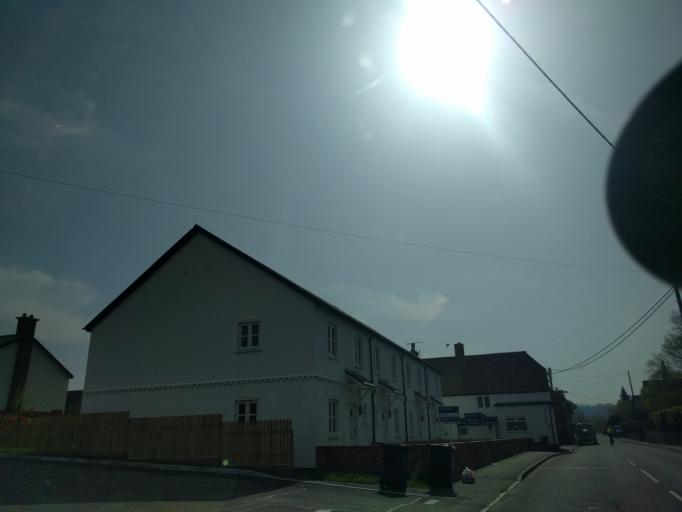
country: GB
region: England
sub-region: Wiltshire
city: Market Lavington
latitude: 51.2829
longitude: -1.9990
